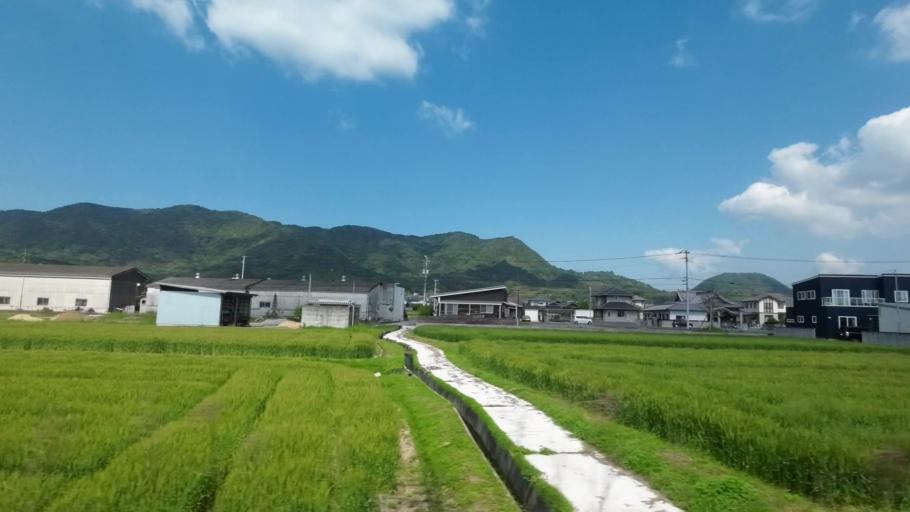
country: JP
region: Kagawa
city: Kan'onjicho
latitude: 34.1757
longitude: 133.6933
